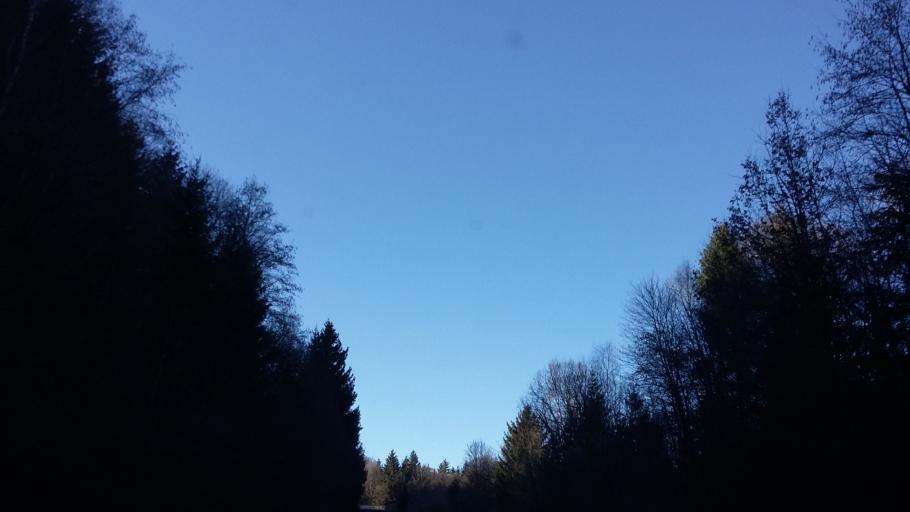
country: DE
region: Bavaria
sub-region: Upper Bavaria
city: Pocking
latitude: 47.9937
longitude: 11.3100
